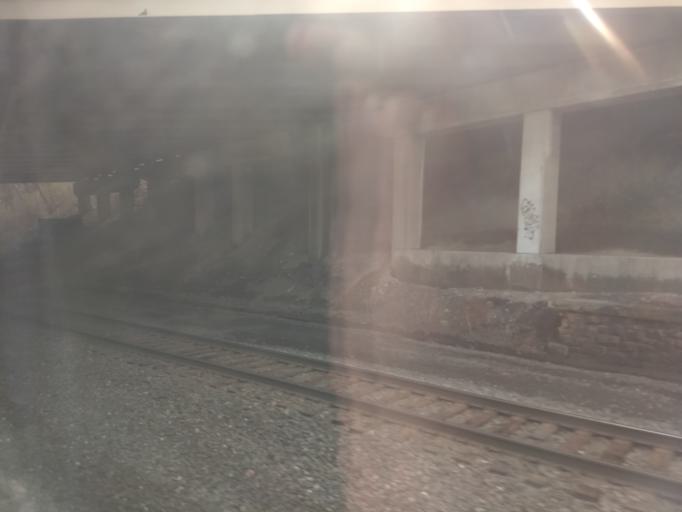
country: US
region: Pennsylvania
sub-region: Blair County
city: Tyrone
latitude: 40.6683
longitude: -78.2384
